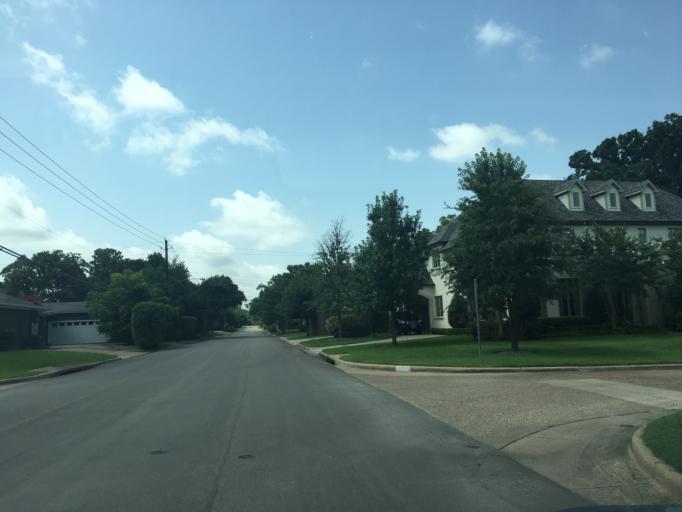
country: US
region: Texas
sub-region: Dallas County
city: University Park
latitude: 32.8906
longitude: -96.7965
